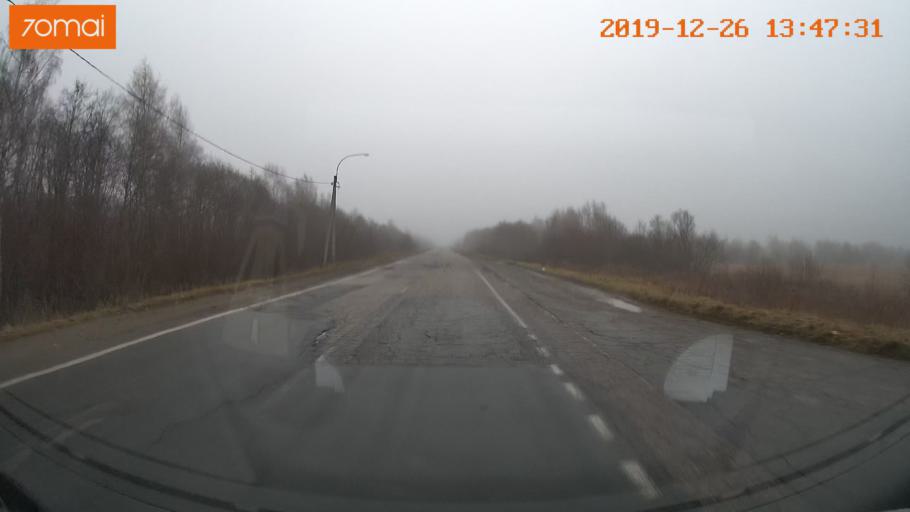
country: RU
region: Vologda
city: Sheksna
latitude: 58.6842
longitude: 38.5350
